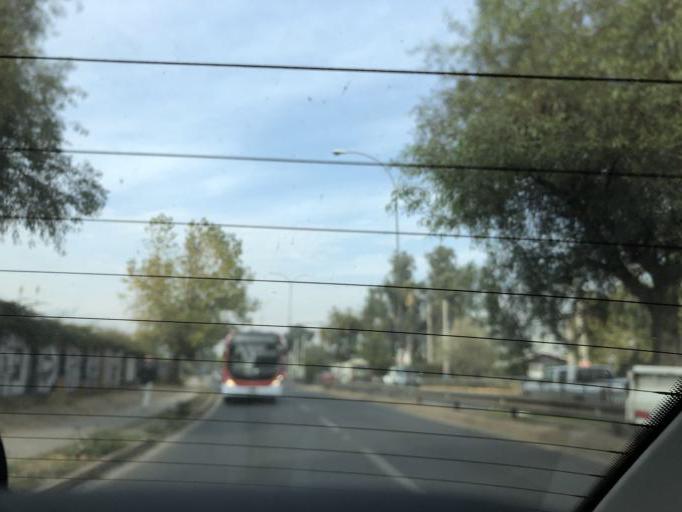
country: CL
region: Santiago Metropolitan
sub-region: Provincia de Cordillera
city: Puente Alto
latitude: -33.5657
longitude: -70.5551
